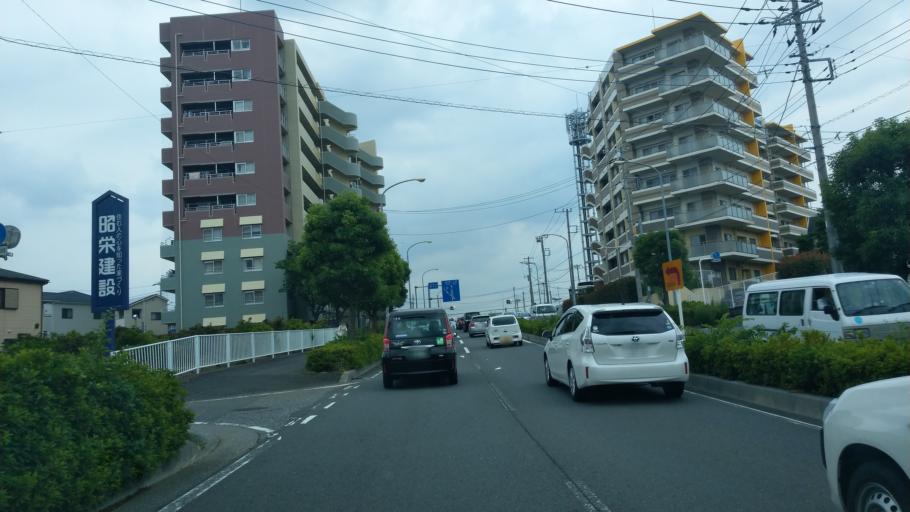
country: JP
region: Saitama
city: Shimotoda
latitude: 35.8569
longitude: 139.6912
